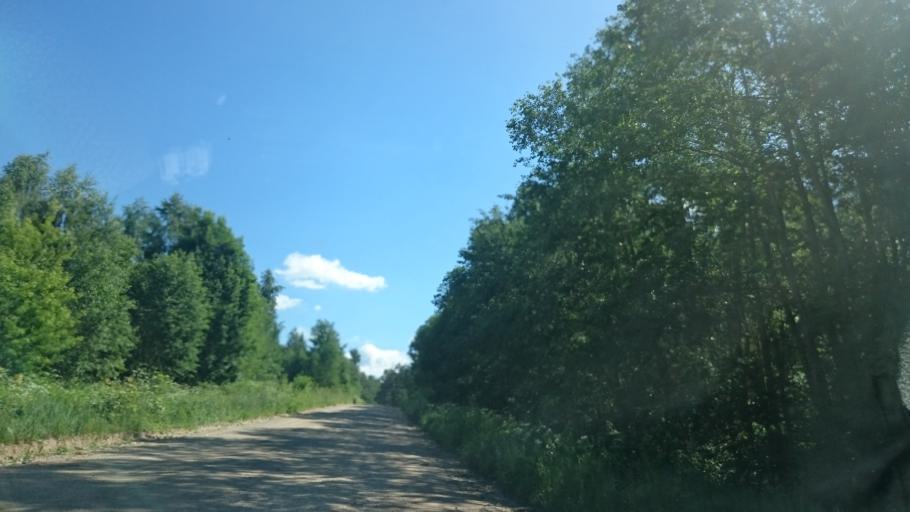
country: LV
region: Cibla
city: Cibla
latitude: 56.5395
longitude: 27.9244
